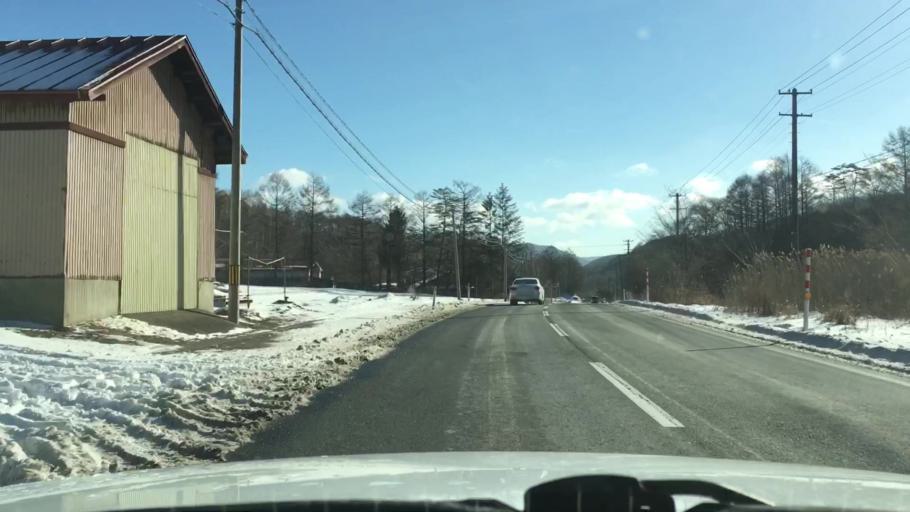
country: JP
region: Iwate
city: Morioka-shi
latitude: 39.6431
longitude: 141.4003
